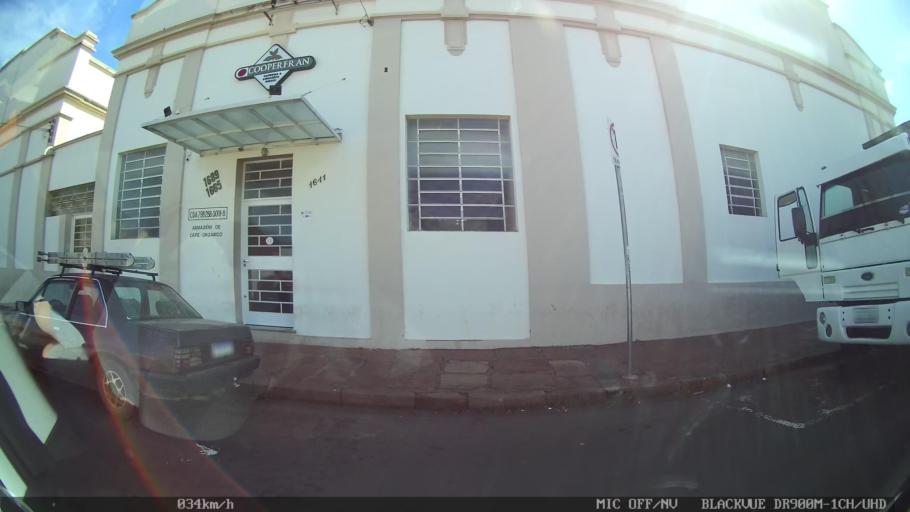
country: BR
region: Sao Paulo
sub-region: Franca
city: Franca
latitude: -20.5364
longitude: -47.4129
